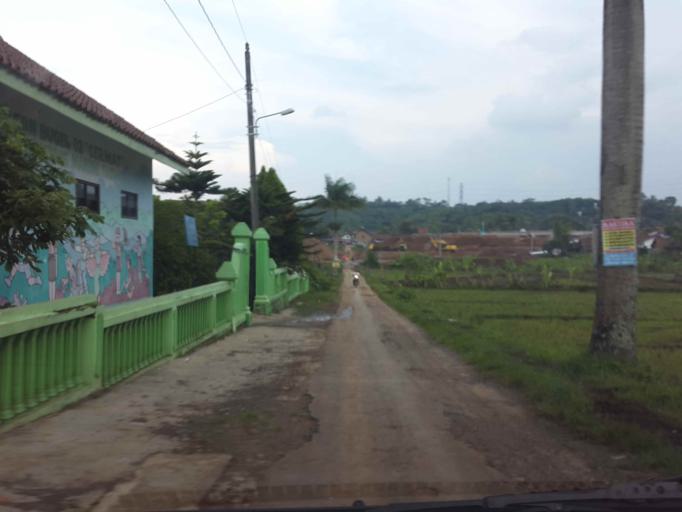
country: ID
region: Central Java
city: Salatiga
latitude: -7.3035
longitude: 110.5065
